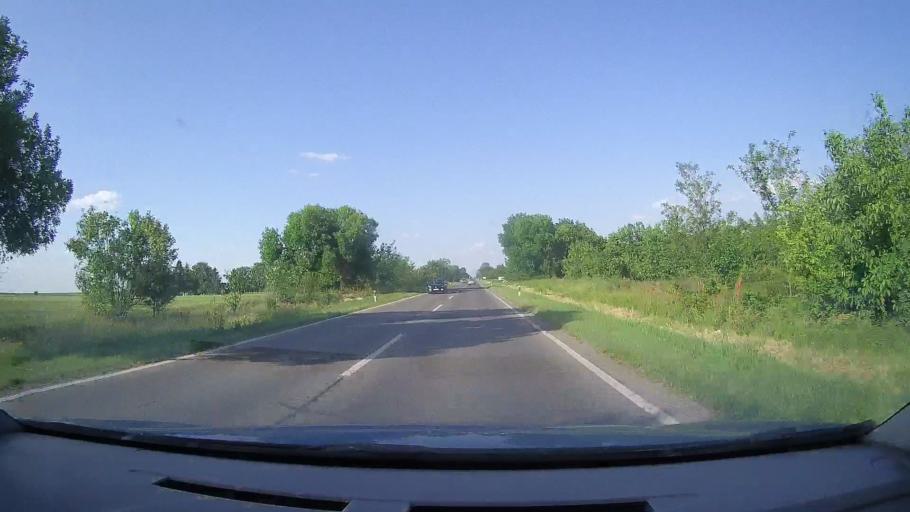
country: RS
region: Autonomna Pokrajina Vojvodina
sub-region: Juznobanatski Okrug
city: Pancevo
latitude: 44.9082
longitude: 20.6943
